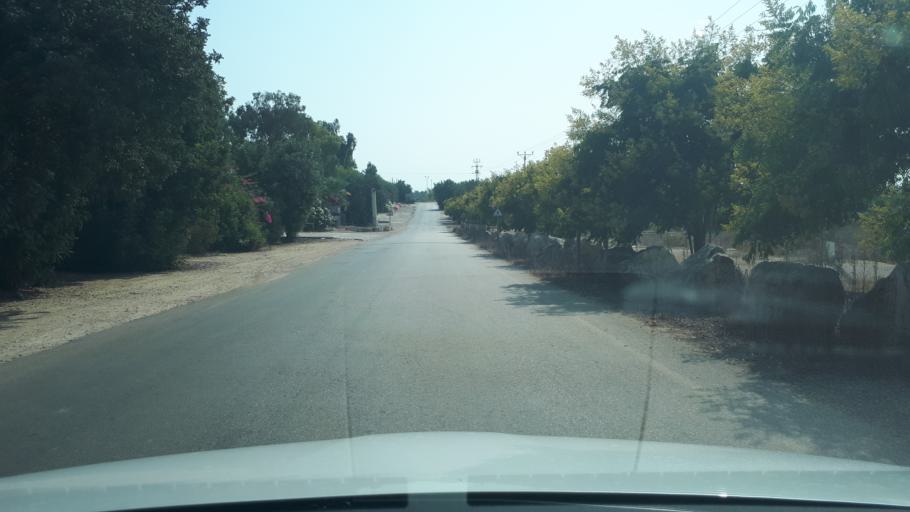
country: IL
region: Central District
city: Rosh Ha'Ayin
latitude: 32.0646
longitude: 34.9466
